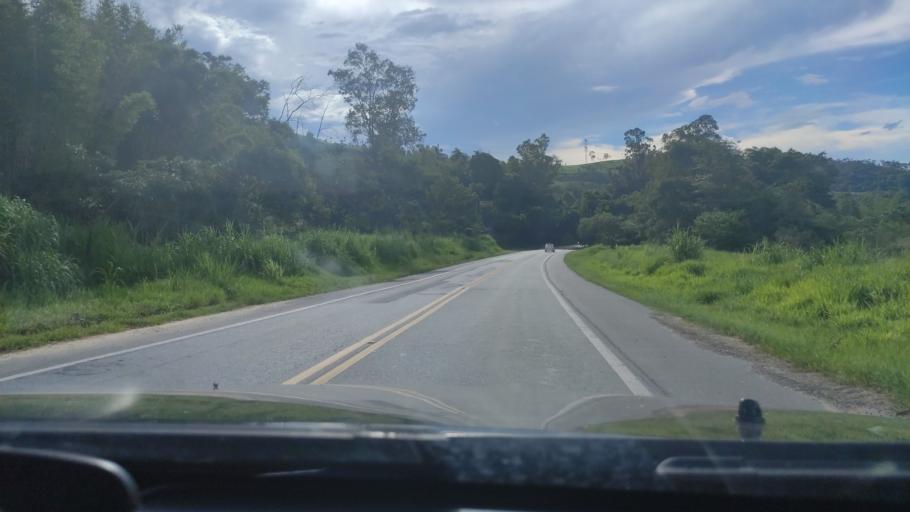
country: BR
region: Sao Paulo
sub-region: Aguas De Lindoia
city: Aguas de Lindoia
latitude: -22.5193
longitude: -46.6613
